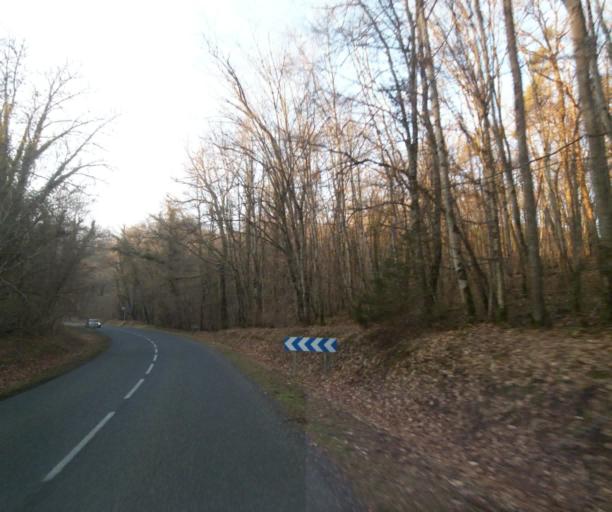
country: FR
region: Champagne-Ardenne
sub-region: Departement de la Haute-Marne
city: Bienville
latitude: 48.6126
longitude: 5.0609
